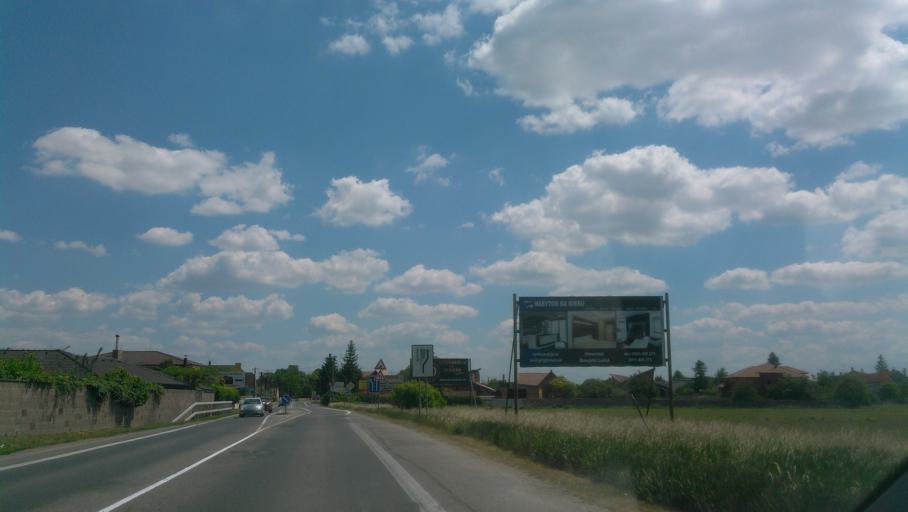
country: SK
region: Bratislavsky
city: Dunajska Luzna
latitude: 48.0900
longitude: 17.2496
